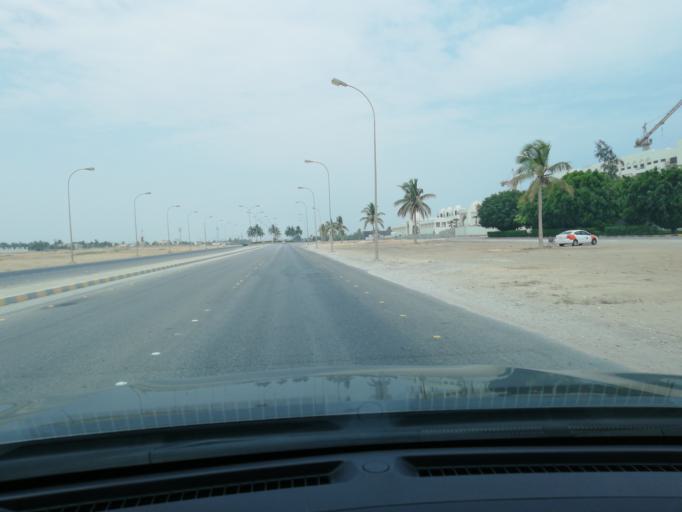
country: OM
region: Zufar
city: Salalah
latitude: 16.9823
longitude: 54.0140
